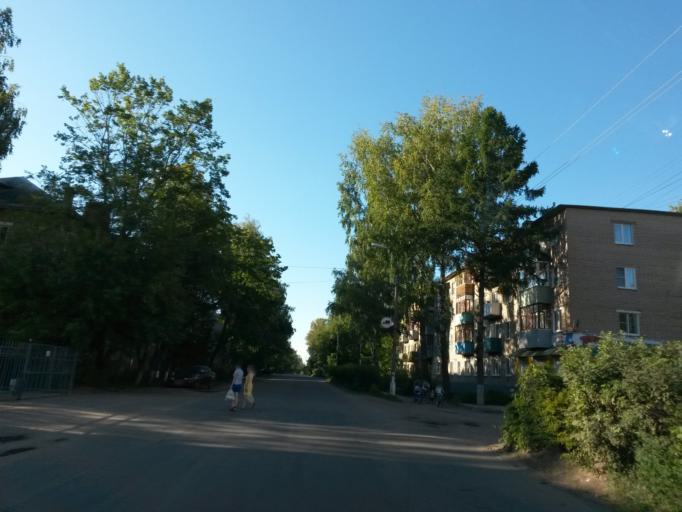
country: RU
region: Jaroslavl
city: Gavrilov-Yam
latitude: 57.3004
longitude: 39.8641
